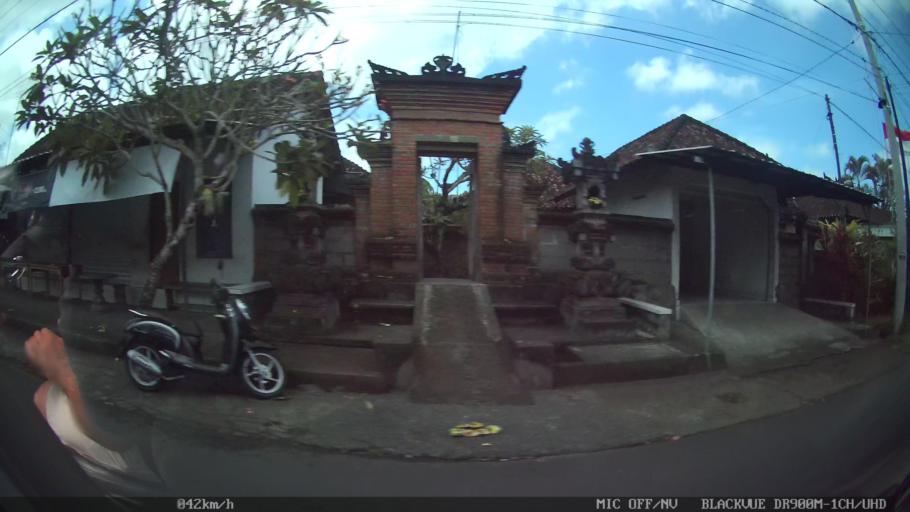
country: ID
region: Bali
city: Banjar Sedang
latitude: -8.5616
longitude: 115.2864
